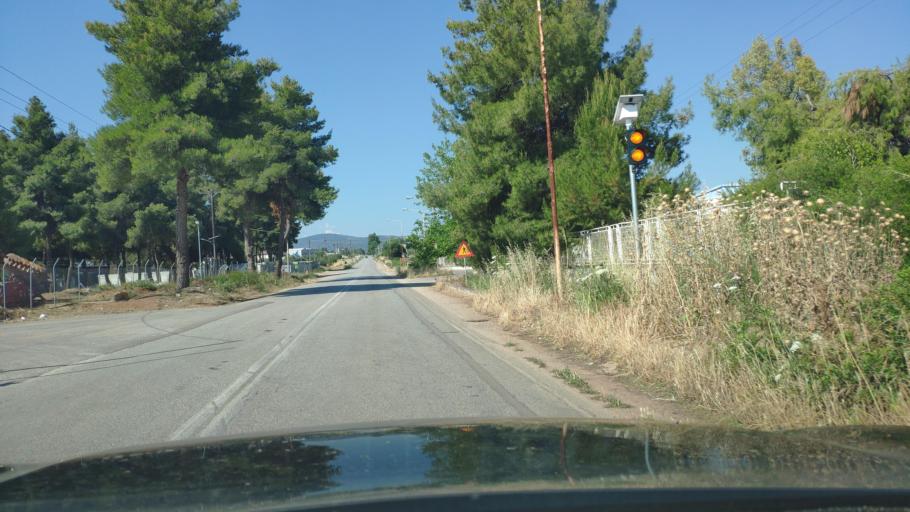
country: GR
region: Central Greece
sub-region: Nomos Voiotias
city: Arma
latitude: 38.3893
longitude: 23.5044
